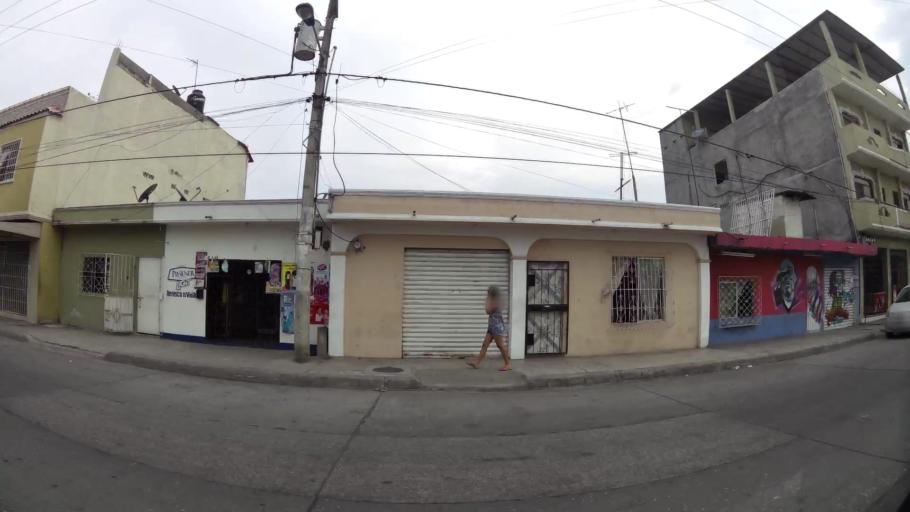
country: EC
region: Guayas
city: Guayaquil
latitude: -2.2553
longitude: -79.8722
